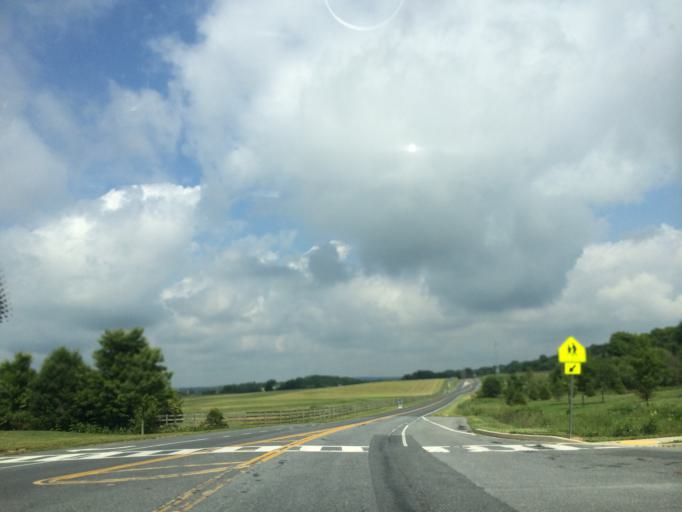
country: US
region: Maryland
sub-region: Carroll County
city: Sykesville
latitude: 39.3025
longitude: -77.0221
